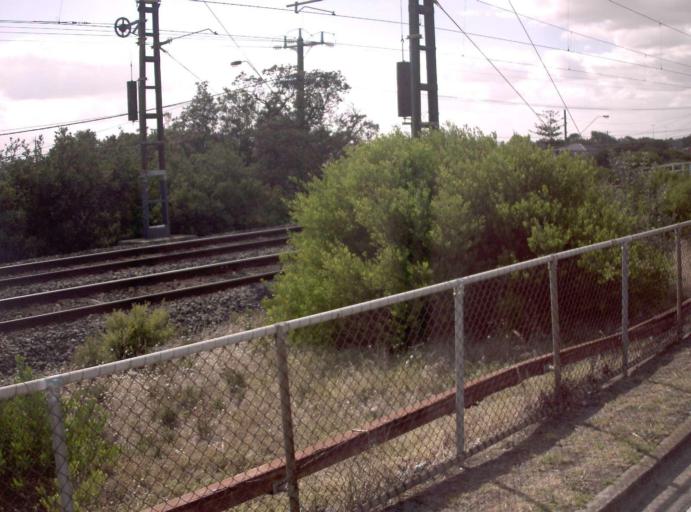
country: AU
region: Victoria
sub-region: Kingston
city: Aspendale
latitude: -38.0175
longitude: 145.0952
